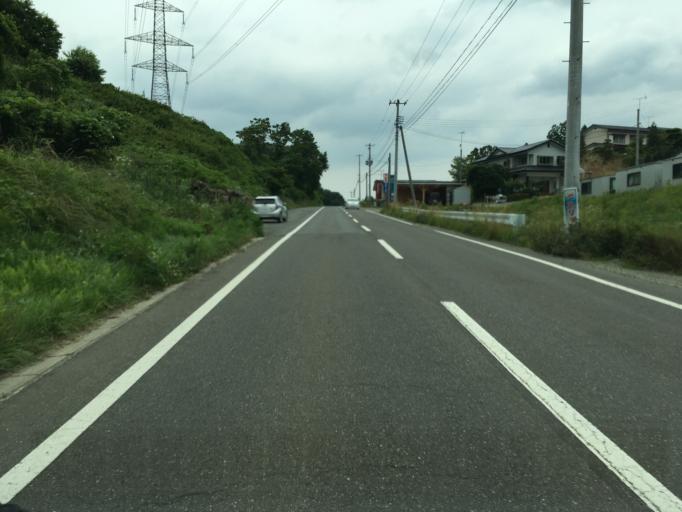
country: JP
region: Fukushima
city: Nihommatsu
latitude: 37.6234
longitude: 140.5395
